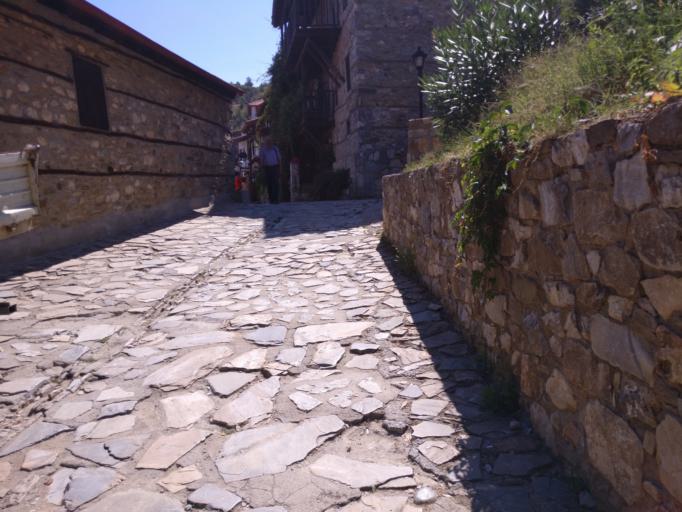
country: GR
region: Central Macedonia
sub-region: Nomos Pierias
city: Leptokarya
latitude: 39.9914
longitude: 22.5708
